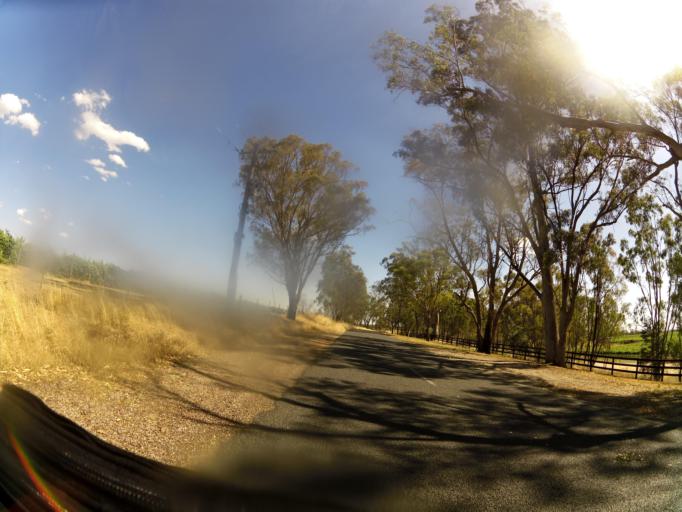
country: AU
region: Victoria
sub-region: Campaspe
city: Kyabram
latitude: -36.8545
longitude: 145.0971
